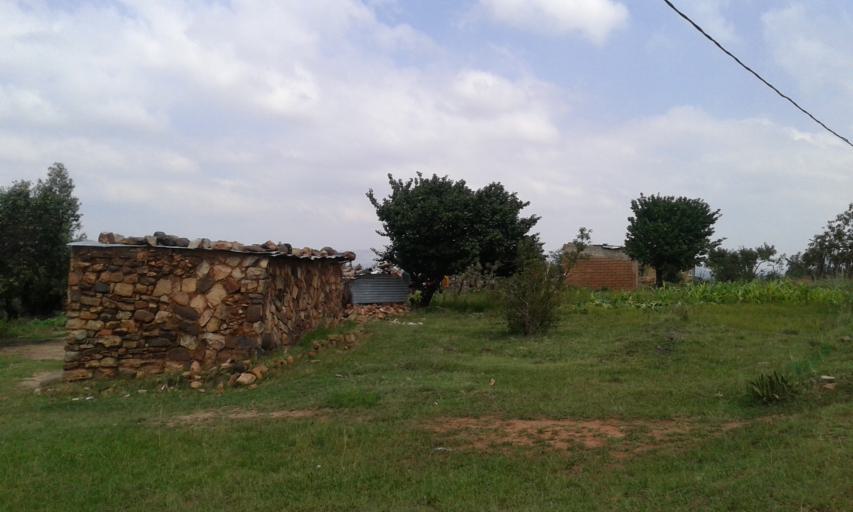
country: LS
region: Maseru
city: Maseru
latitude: -29.4303
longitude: 27.5752
